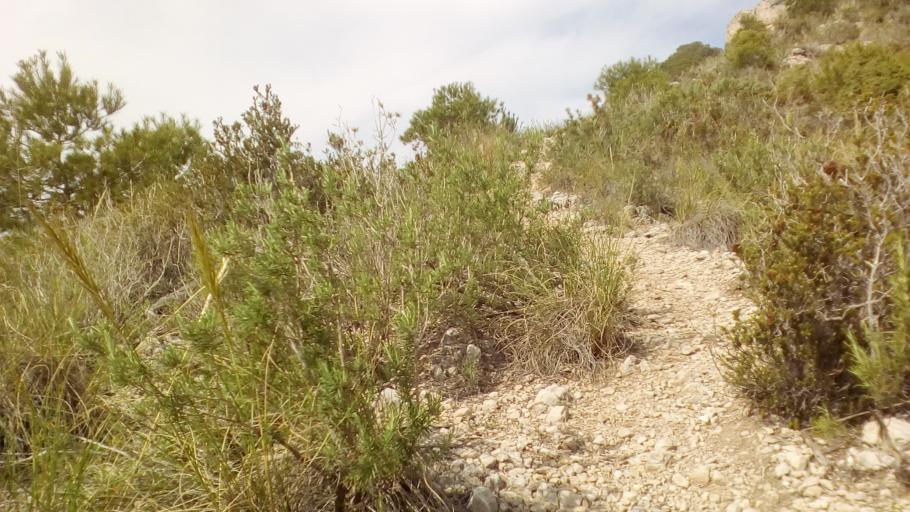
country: ES
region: Valencia
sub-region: Provincia de Valencia
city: Xeraco,Jaraco
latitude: 39.0382
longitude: -0.2378
